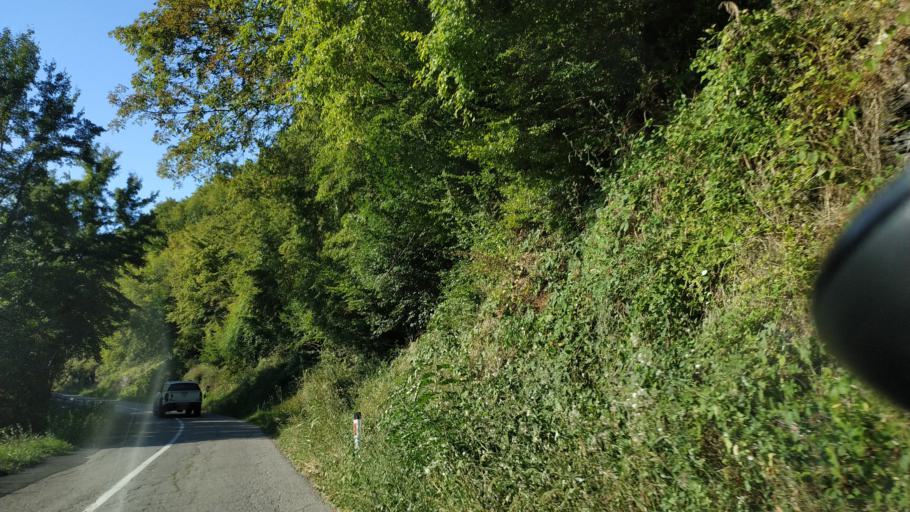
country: RS
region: Central Serbia
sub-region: Rasinski Okrug
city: Krusevac
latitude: 43.4624
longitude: 21.3611
